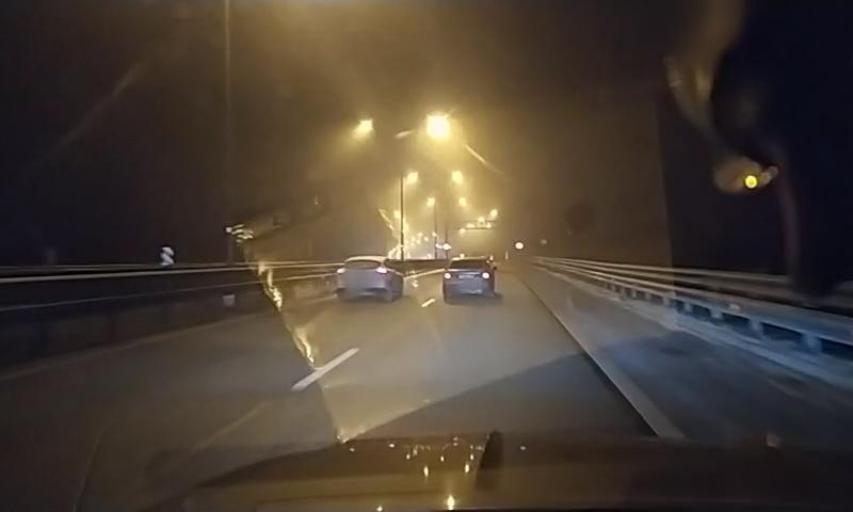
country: RU
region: Leningrad
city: Bugry
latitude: 60.1153
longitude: 30.3865
